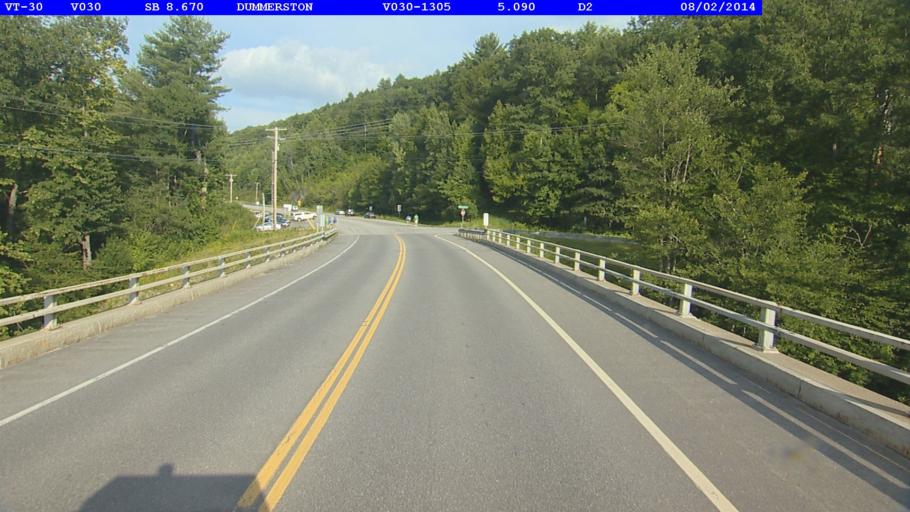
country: US
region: Vermont
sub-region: Windham County
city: Newfane
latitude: 42.9473
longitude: -72.6415
